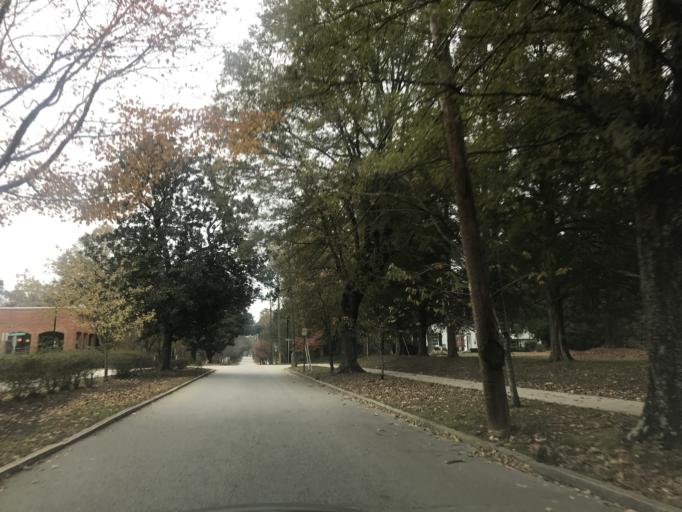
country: US
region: North Carolina
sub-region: Wake County
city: Wake Forest
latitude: 35.9849
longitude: -78.5081
